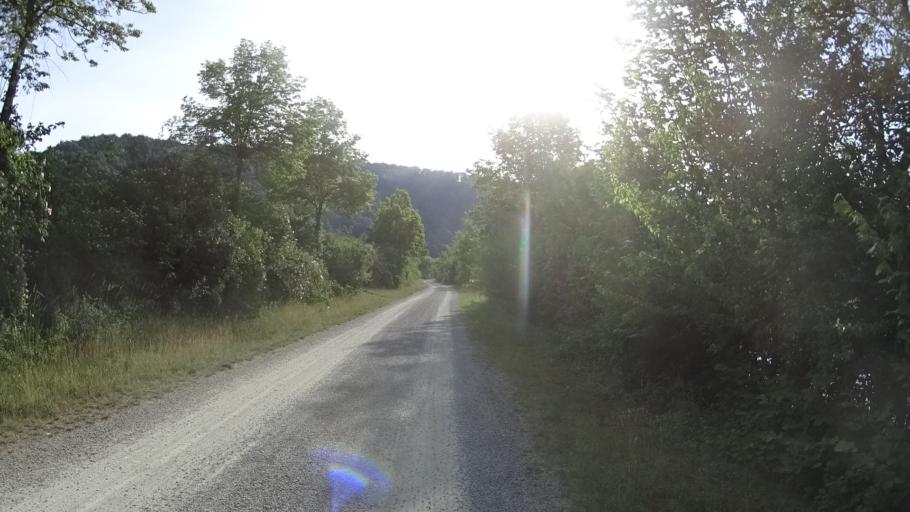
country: DE
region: Bavaria
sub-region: Lower Bavaria
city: Riedenburg
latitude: 48.9919
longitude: 11.6777
